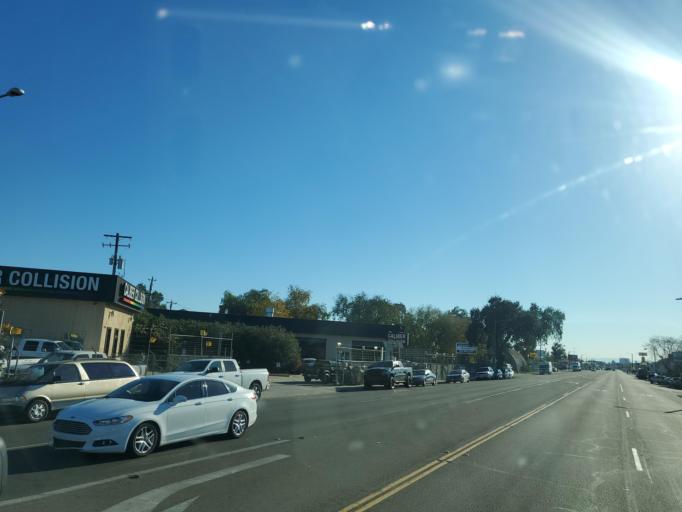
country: US
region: California
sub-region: San Joaquin County
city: August
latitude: 37.9876
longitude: -121.2690
